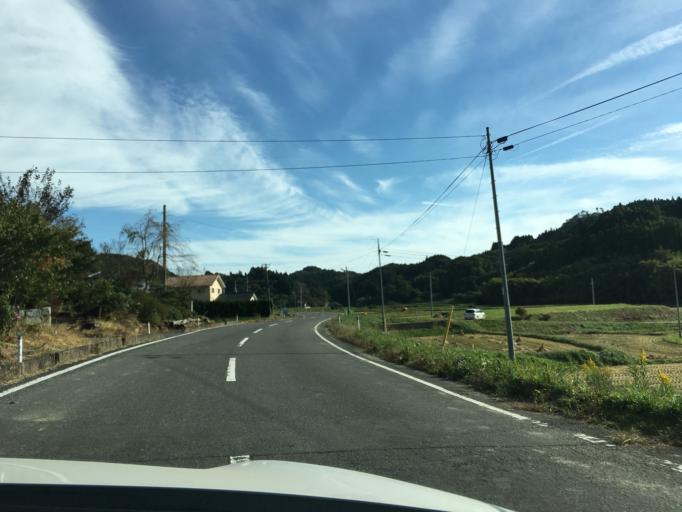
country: JP
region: Fukushima
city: Miharu
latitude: 37.3357
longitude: 140.4876
